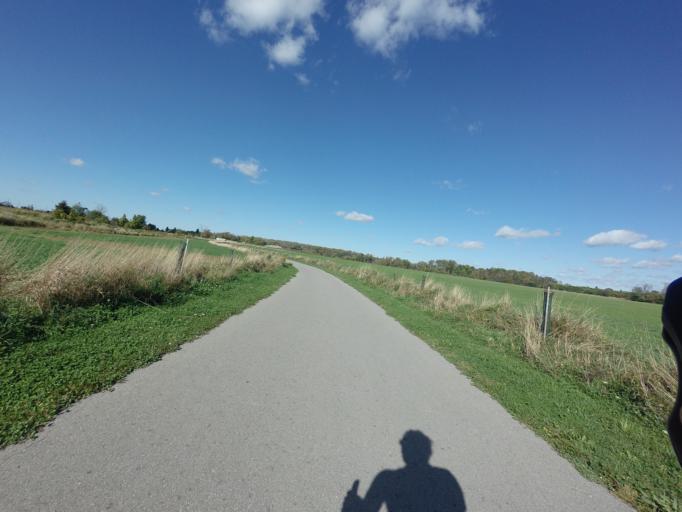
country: CA
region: Ontario
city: Ajax
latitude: 43.8482
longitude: -78.9710
